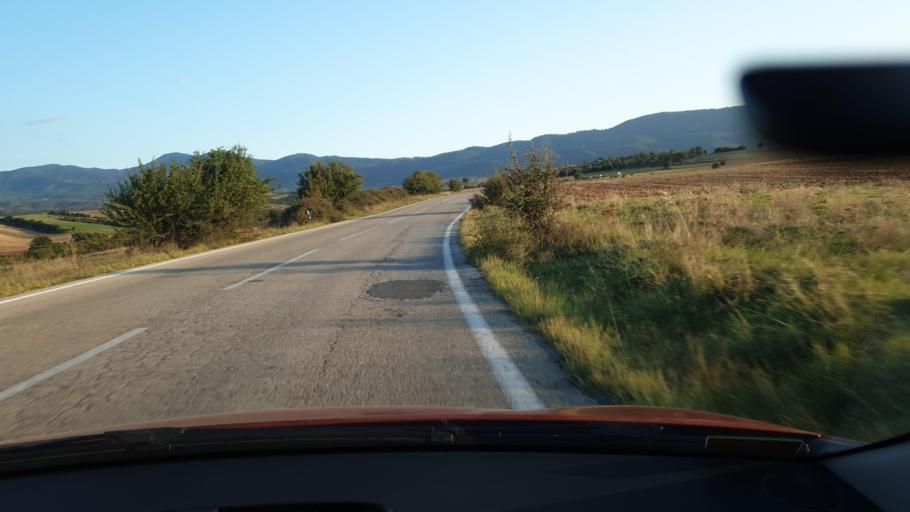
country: GR
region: Central Macedonia
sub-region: Nomos Thessalonikis
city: Nea Apollonia
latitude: 40.5323
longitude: 23.4706
